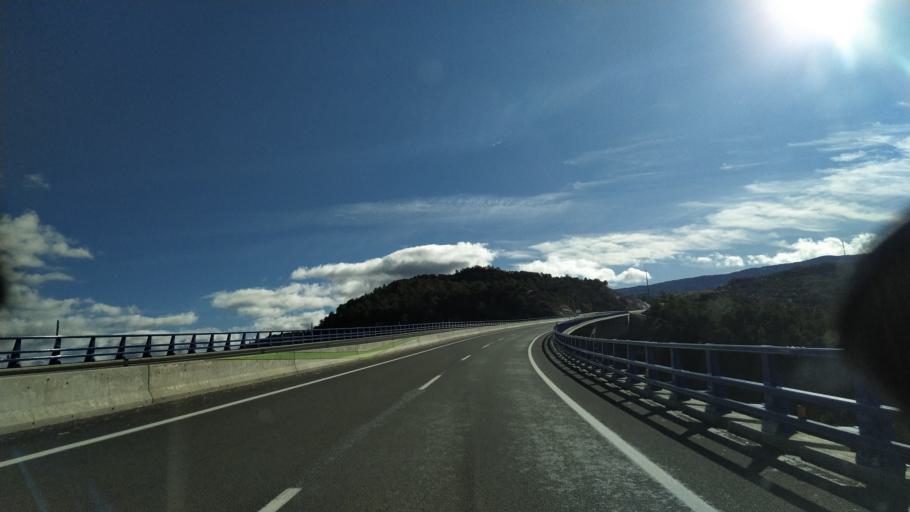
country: ES
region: Aragon
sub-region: Provincia de Huesca
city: Arguis
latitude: 42.4038
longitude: -0.3758
